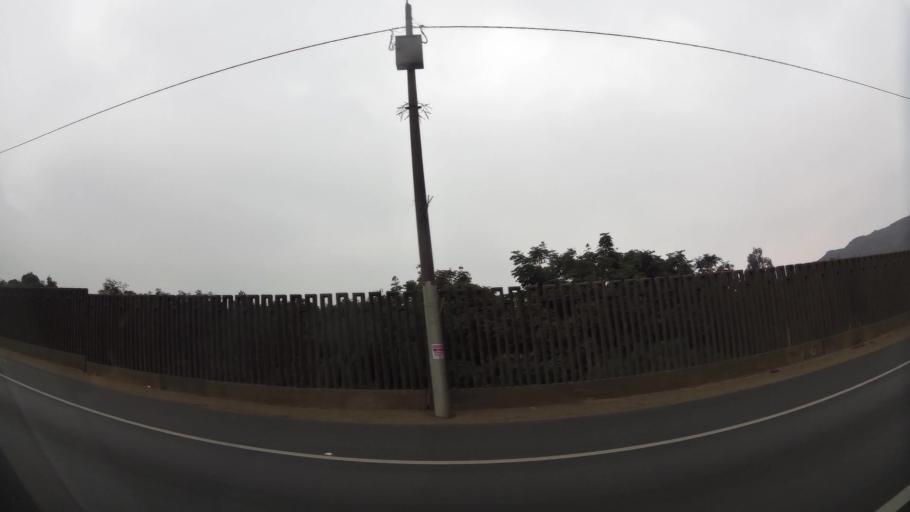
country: PE
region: Lima
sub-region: Lima
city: Vitarte
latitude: -12.0280
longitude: -76.9737
